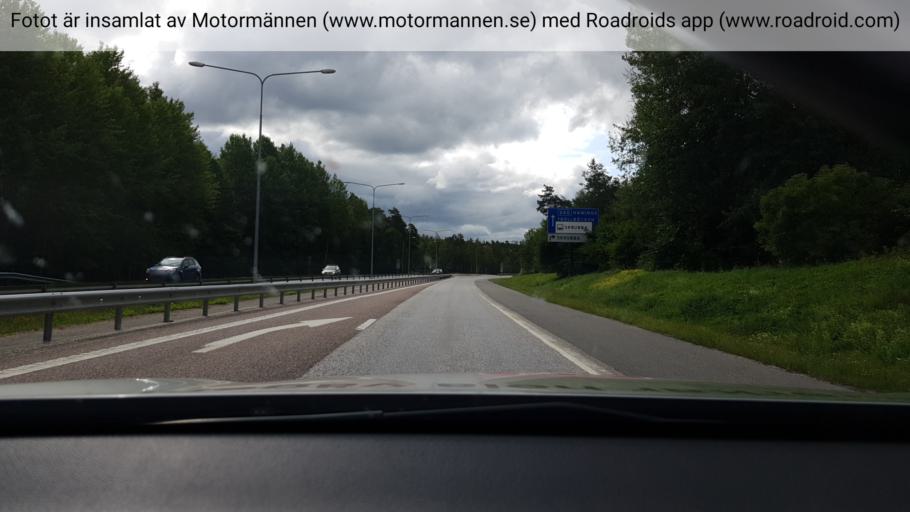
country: SE
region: Stockholm
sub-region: Nacka Kommun
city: Alta
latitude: 59.2438
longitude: 18.1832
